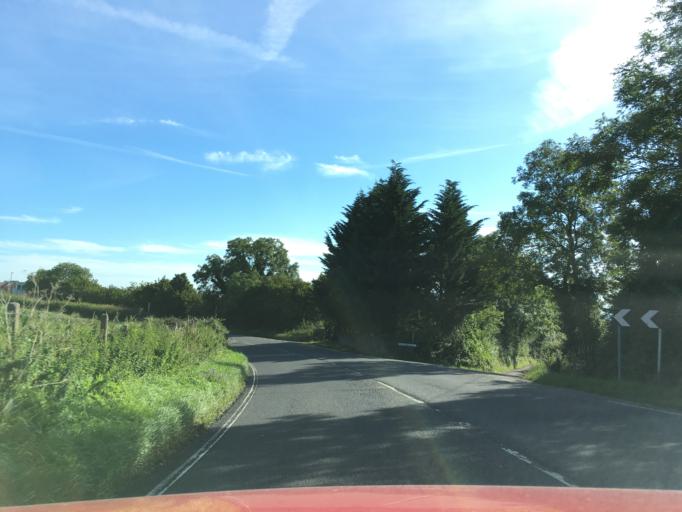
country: GB
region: England
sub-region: Bath and North East Somerset
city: Compton Dando
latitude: 51.3984
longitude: -2.5172
